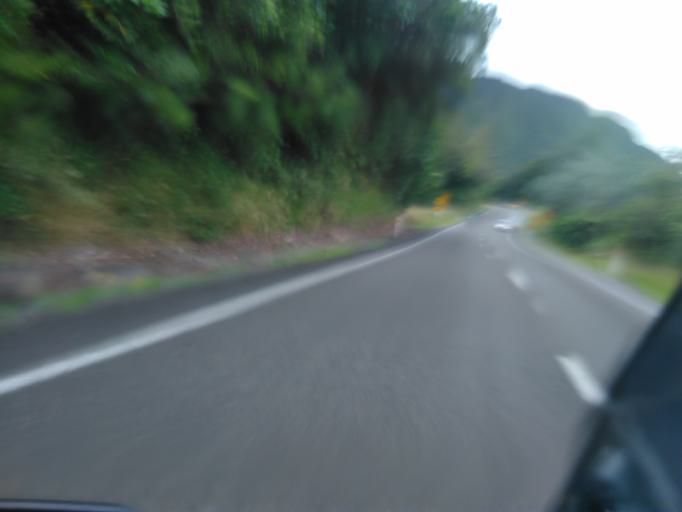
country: NZ
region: Bay of Plenty
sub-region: Opotiki District
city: Opotiki
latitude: -38.2378
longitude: 177.3076
